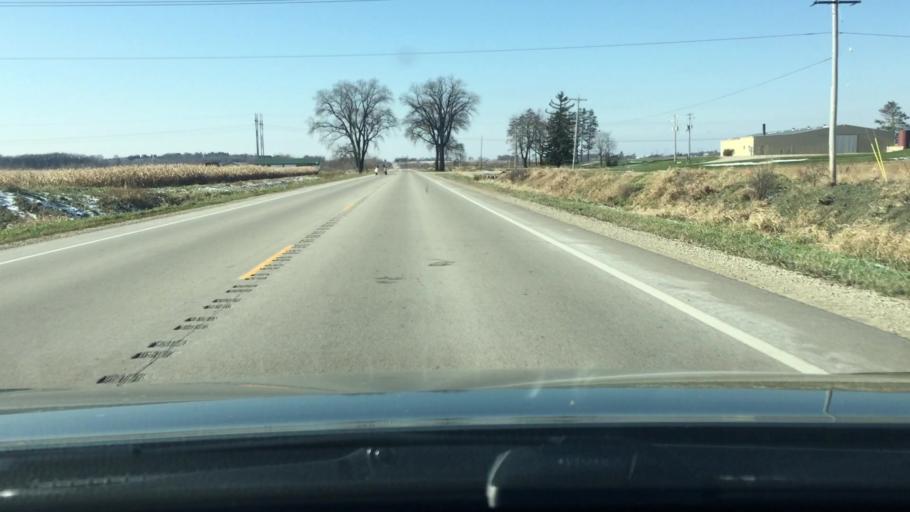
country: US
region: Wisconsin
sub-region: Jefferson County
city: Jefferson
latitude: 43.0071
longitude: -88.8616
